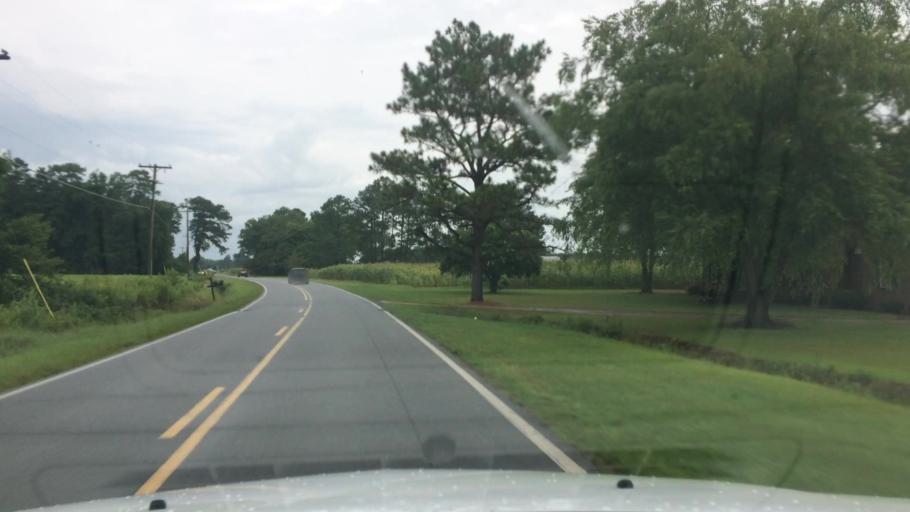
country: US
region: North Carolina
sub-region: Pitt County
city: Farmville
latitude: 35.5535
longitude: -77.5450
